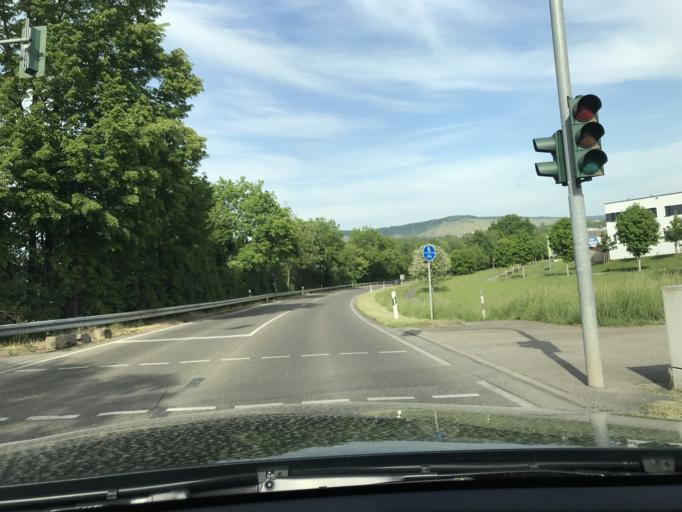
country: DE
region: Baden-Wuerttemberg
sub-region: Regierungsbezirk Stuttgart
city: Waiblingen
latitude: 48.8246
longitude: 9.3207
